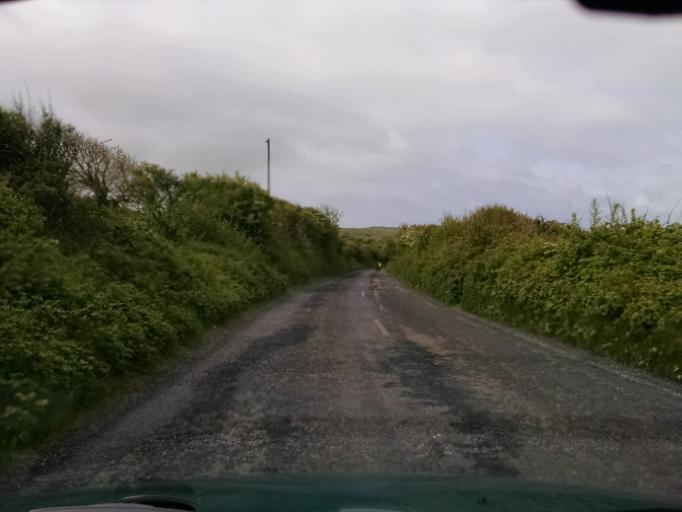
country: IE
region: Connaught
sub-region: County Galway
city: Bearna
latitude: 53.0521
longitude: -9.3432
